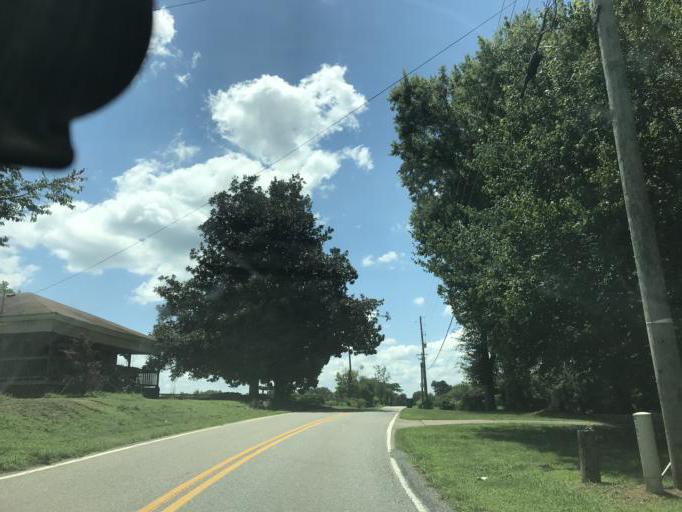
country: US
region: Georgia
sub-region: Fulton County
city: Milton
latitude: 34.2305
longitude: -84.2564
